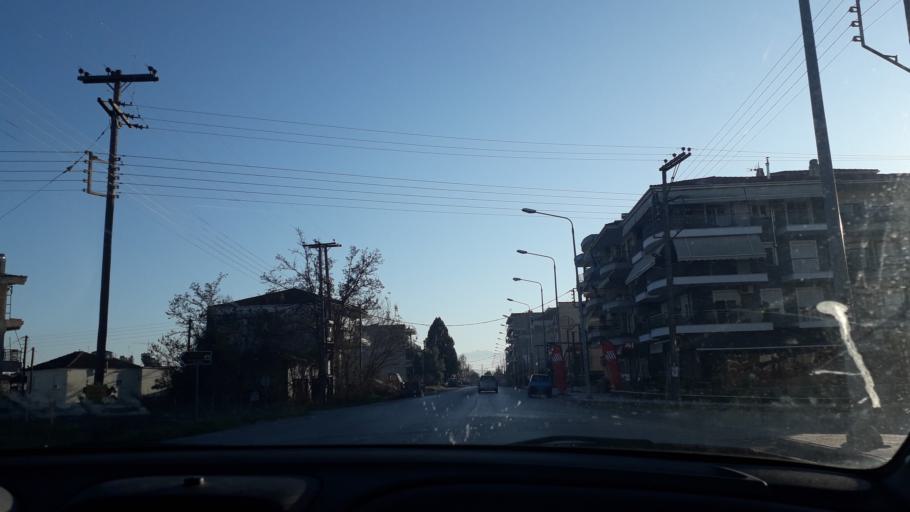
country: GR
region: Central Macedonia
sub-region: Nomos Imathias
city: Alexandreia
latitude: 40.6256
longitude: 22.4480
